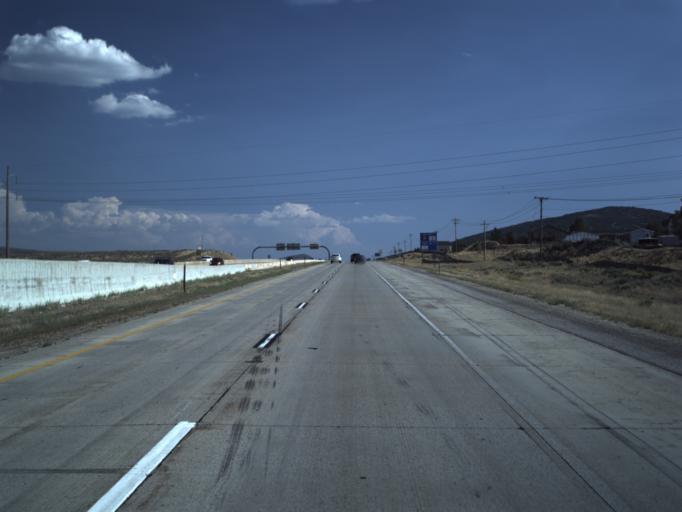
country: US
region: Utah
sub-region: Summit County
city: Snyderville
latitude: 40.7277
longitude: -111.4948
